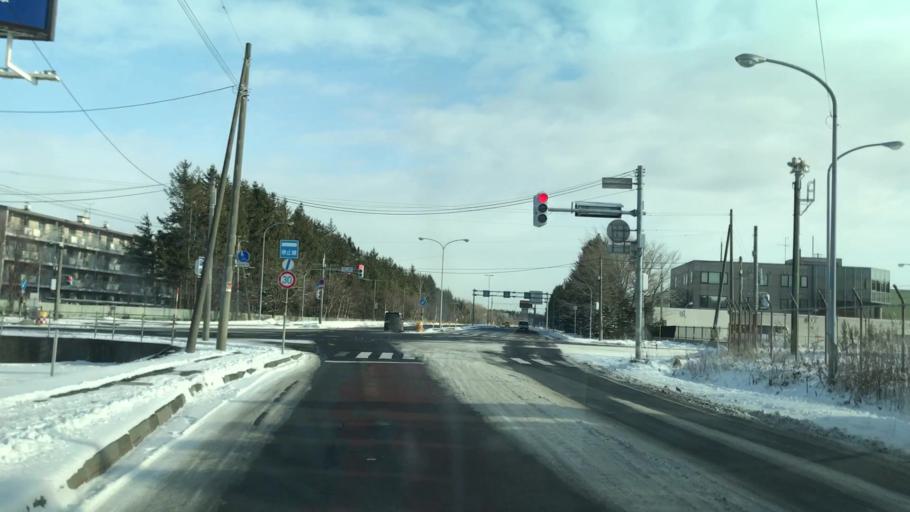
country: JP
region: Hokkaido
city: Chitose
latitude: 42.8148
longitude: 141.6498
